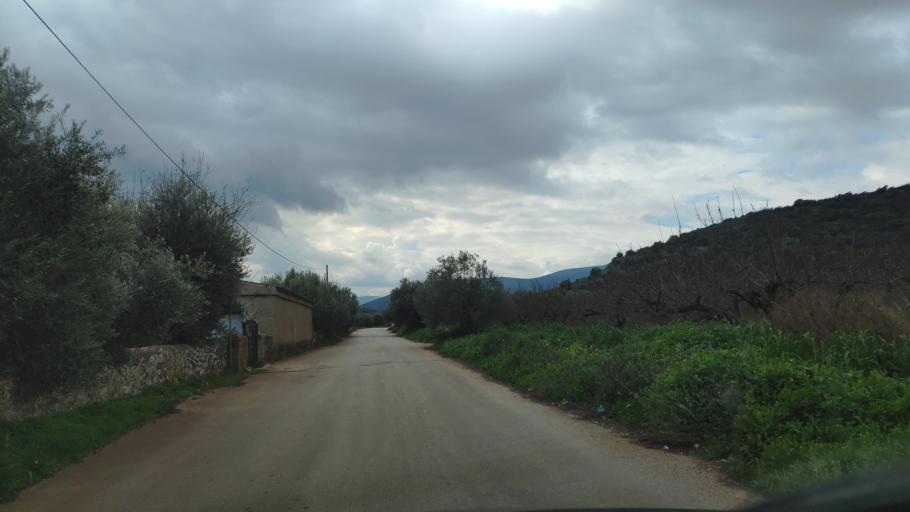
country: GR
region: Peloponnese
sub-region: Nomos Argolidos
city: Nea Kios
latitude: 37.5462
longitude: 22.7134
